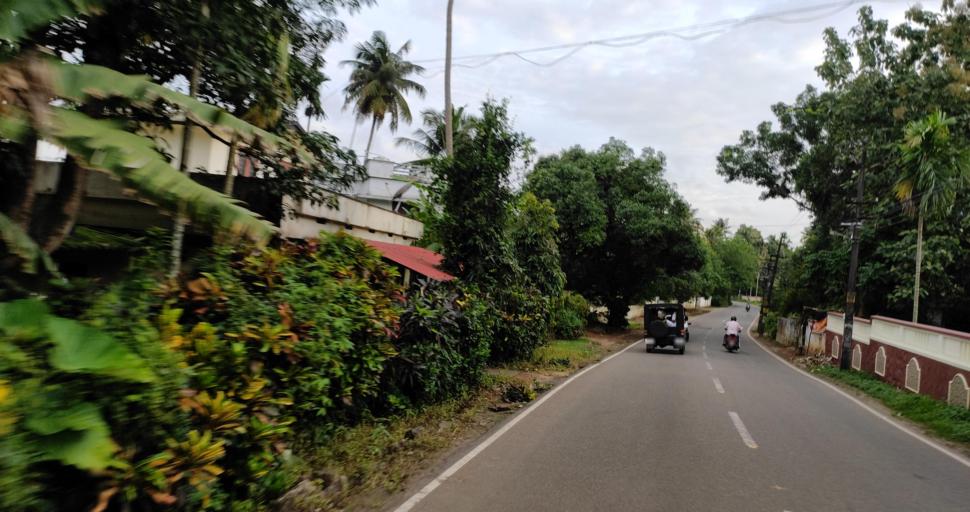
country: IN
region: Kerala
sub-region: Thrissur District
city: Kizhake Chalakudi
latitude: 10.3186
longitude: 76.3569
